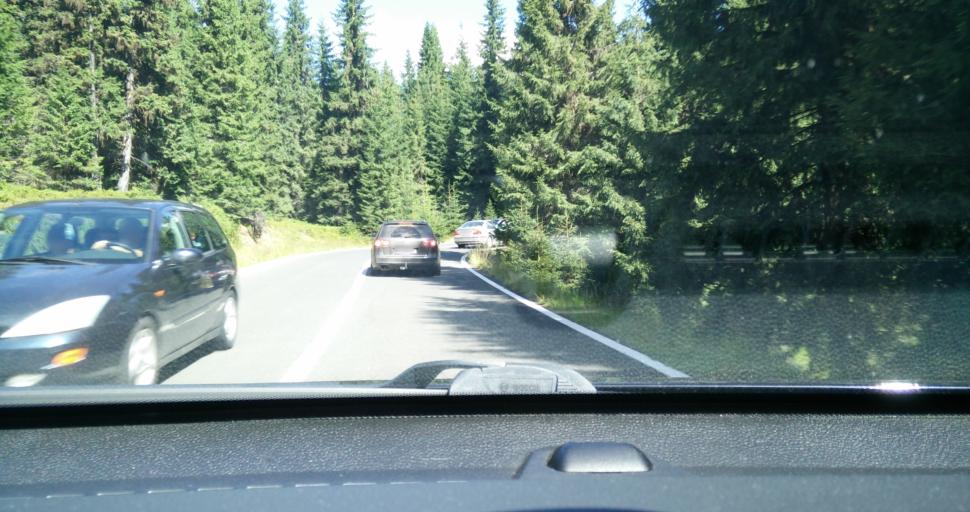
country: RO
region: Hunedoara
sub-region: Oras Petrila
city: Petrila
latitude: 45.4676
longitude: 23.6308
